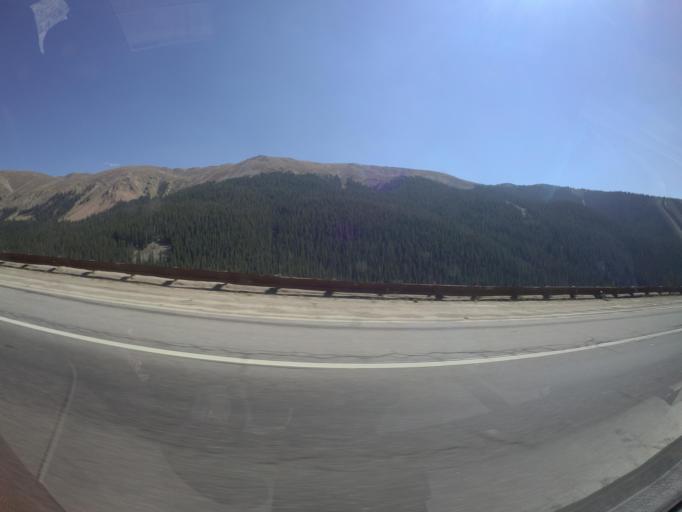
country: US
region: Colorado
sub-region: Summit County
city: Keystone
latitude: 39.6747
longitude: -105.9636
